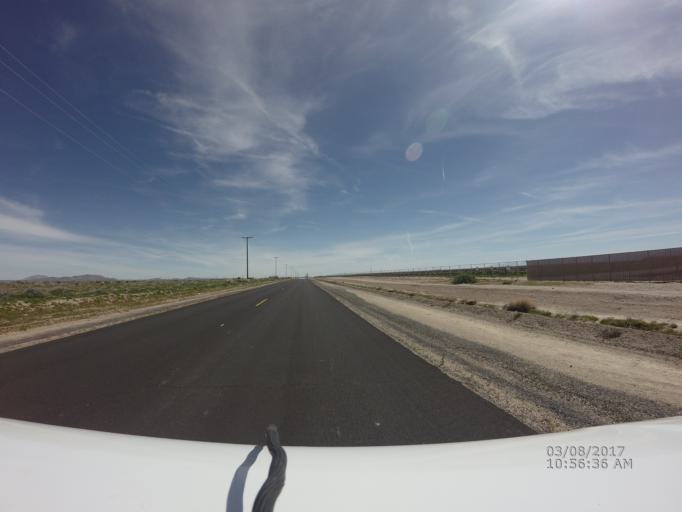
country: US
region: California
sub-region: Los Angeles County
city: Green Valley
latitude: 34.8193
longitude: -118.3692
